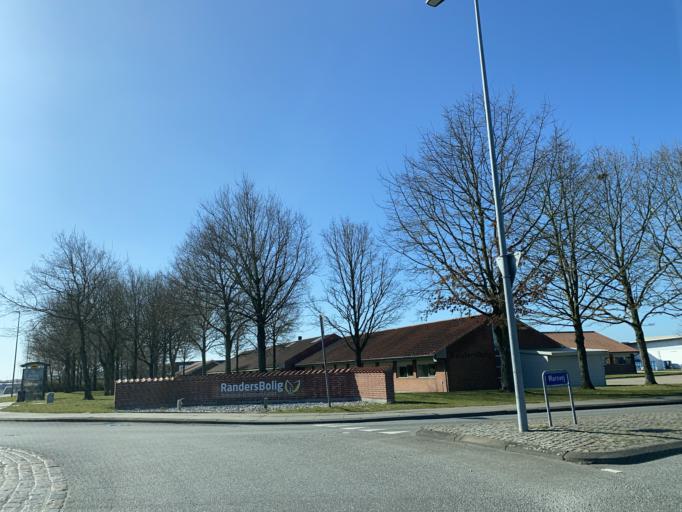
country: DK
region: Central Jutland
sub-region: Randers Kommune
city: Randers
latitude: 56.4282
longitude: 10.0618
